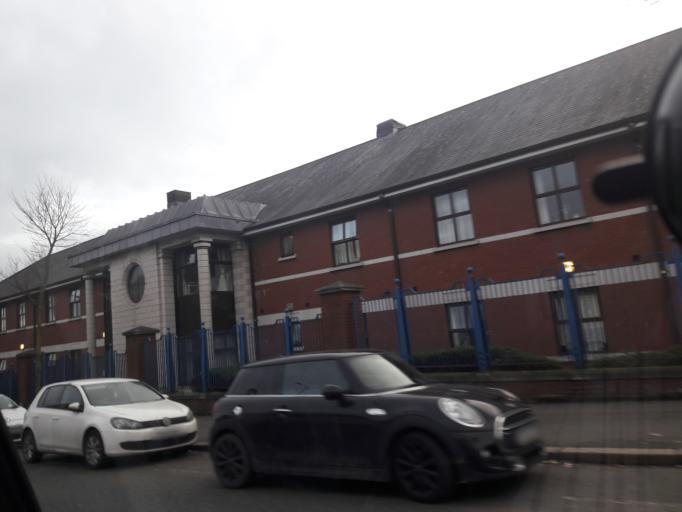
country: GB
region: Northern Ireland
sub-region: City of Belfast
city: Belfast
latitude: 54.6079
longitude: -5.9380
